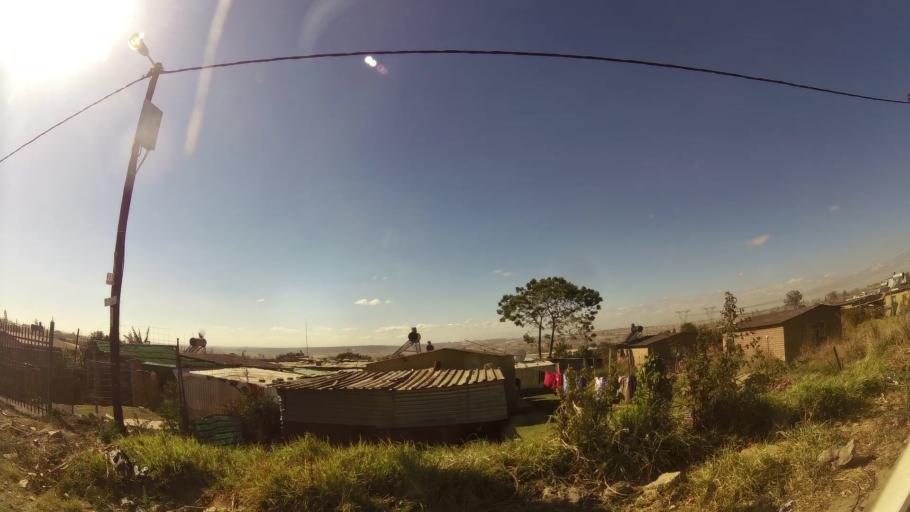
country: ZA
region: Gauteng
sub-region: City of Johannesburg Metropolitan Municipality
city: Diepsloot
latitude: -25.9191
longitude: 28.0843
